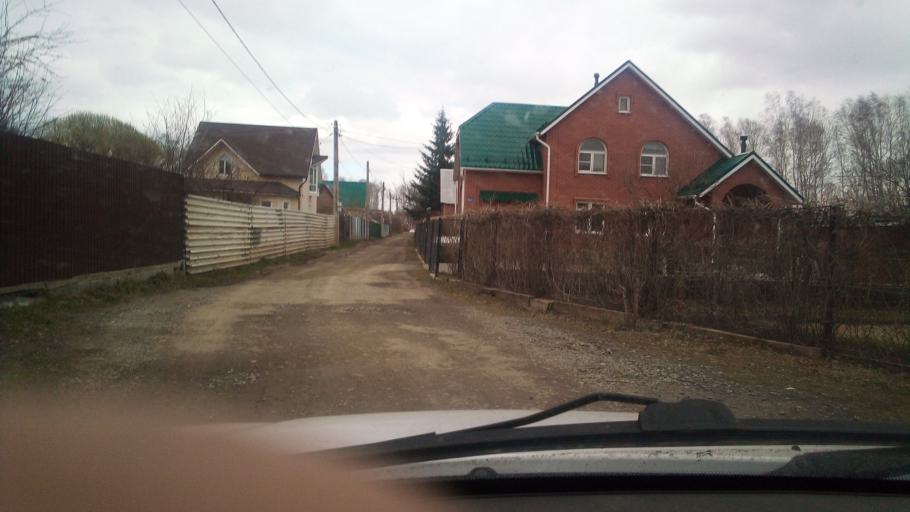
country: RU
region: Chelyabinsk
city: Sargazy
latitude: 55.1287
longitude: 61.2420
